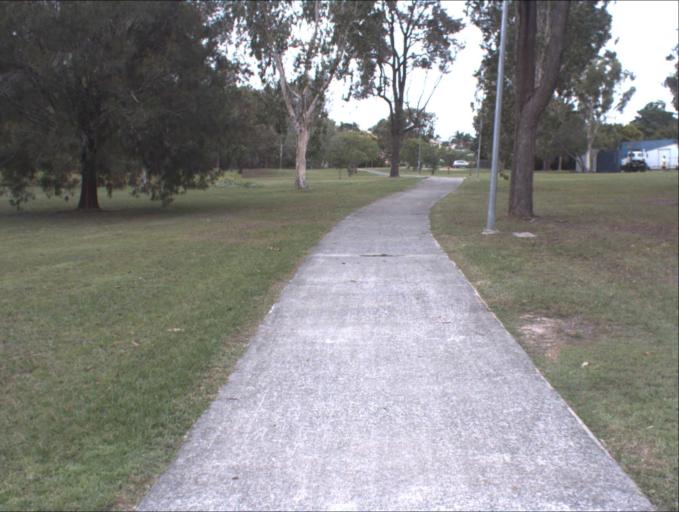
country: AU
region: Queensland
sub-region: Brisbane
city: Sunnybank Hills
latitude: -27.6603
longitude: 153.0257
